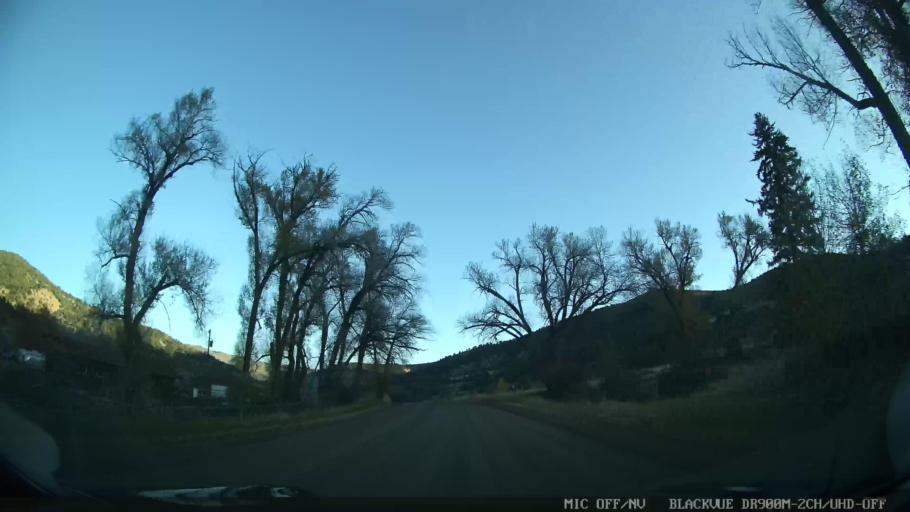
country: US
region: Colorado
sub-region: Grand County
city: Kremmling
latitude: 39.9303
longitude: -106.5266
